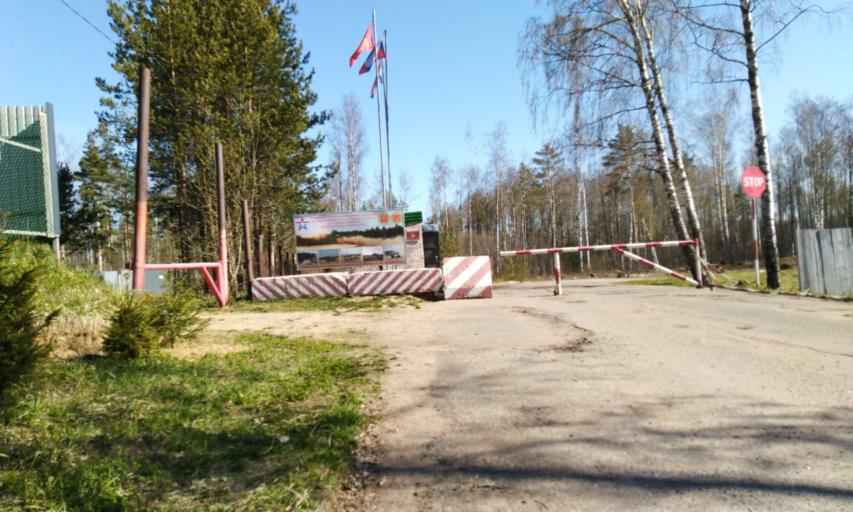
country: RU
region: Leningrad
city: Garbolovo
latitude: 60.3930
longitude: 30.4892
